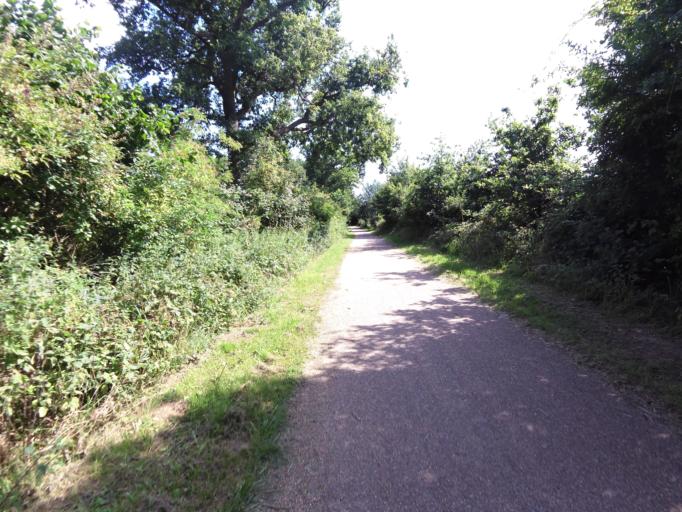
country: GB
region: England
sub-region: Essex
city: Colchester
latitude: 51.9039
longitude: 0.9115
